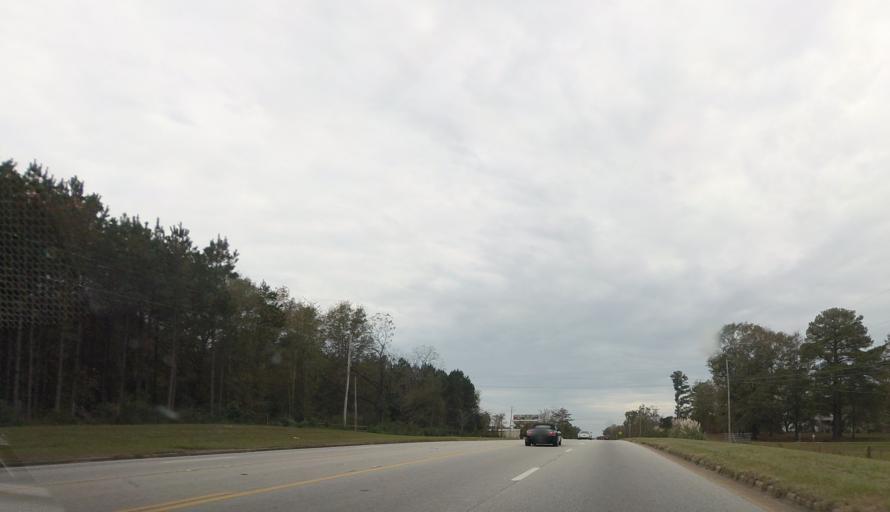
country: US
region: Alabama
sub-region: Lee County
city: Opelika
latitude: 32.6412
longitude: -85.3200
